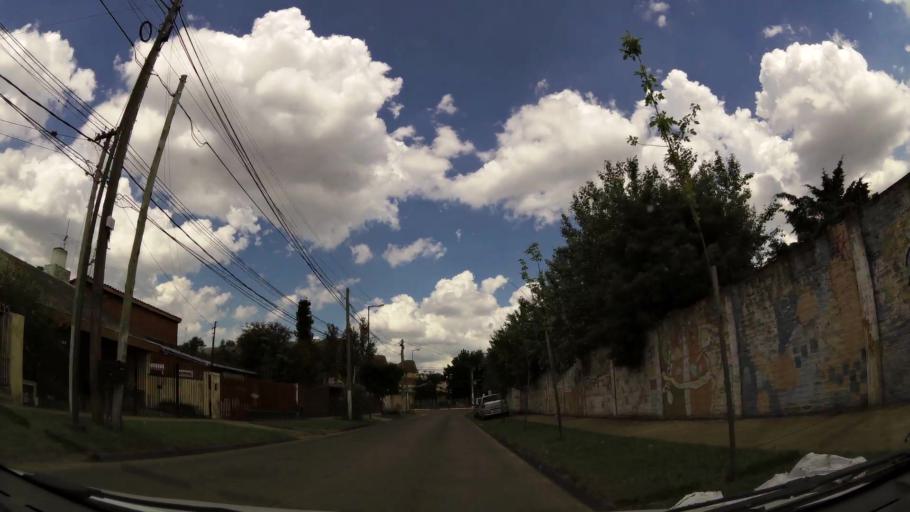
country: AR
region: Buenos Aires
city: Ituzaingo
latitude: -34.6490
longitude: -58.6774
